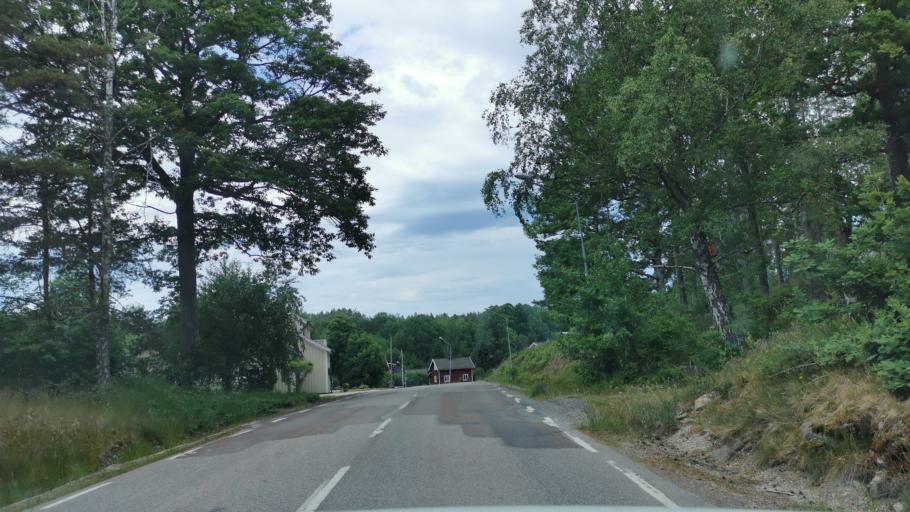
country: SE
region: Vaestra Goetaland
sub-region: Melleruds Kommun
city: Mellerud
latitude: 58.8248
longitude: 12.4136
